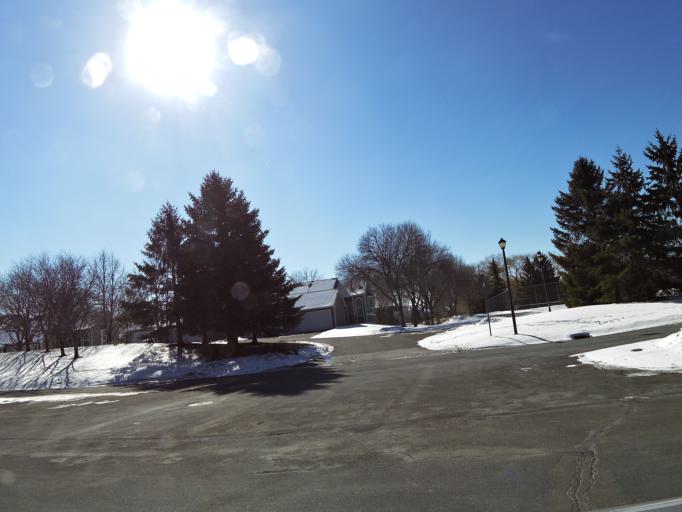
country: US
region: Minnesota
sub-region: Washington County
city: Woodbury
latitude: 44.9352
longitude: -92.9316
